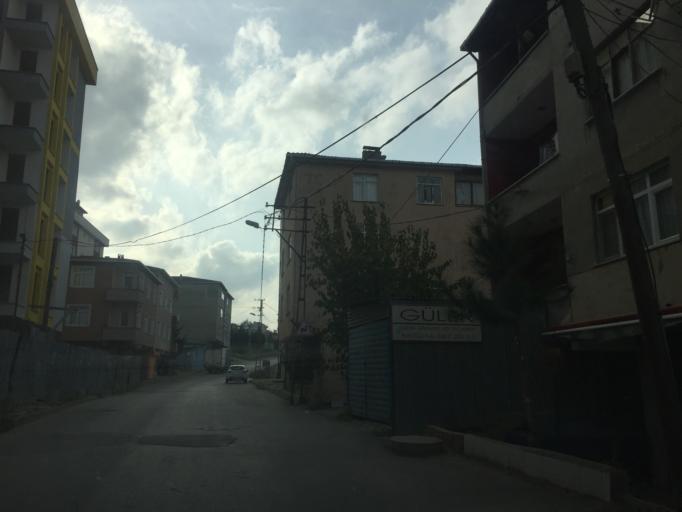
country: TR
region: Istanbul
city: Sultanbeyli
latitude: 40.9415
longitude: 29.2990
